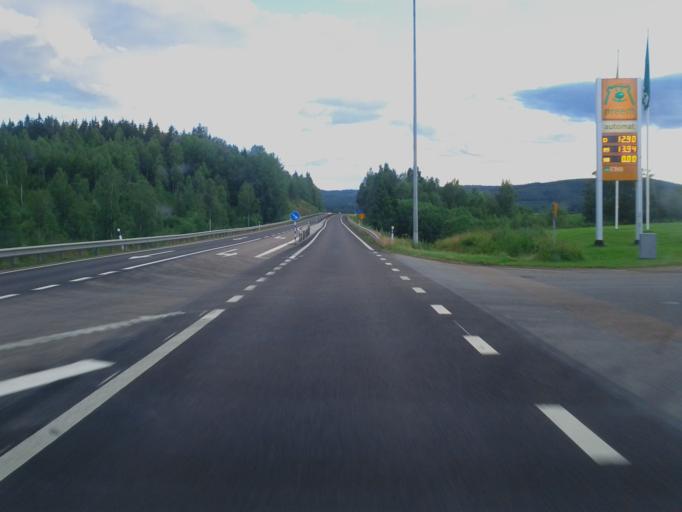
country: SE
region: Dalarna
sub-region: Borlange Kommun
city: Borlaenge
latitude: 60.4324
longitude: 15.3408
